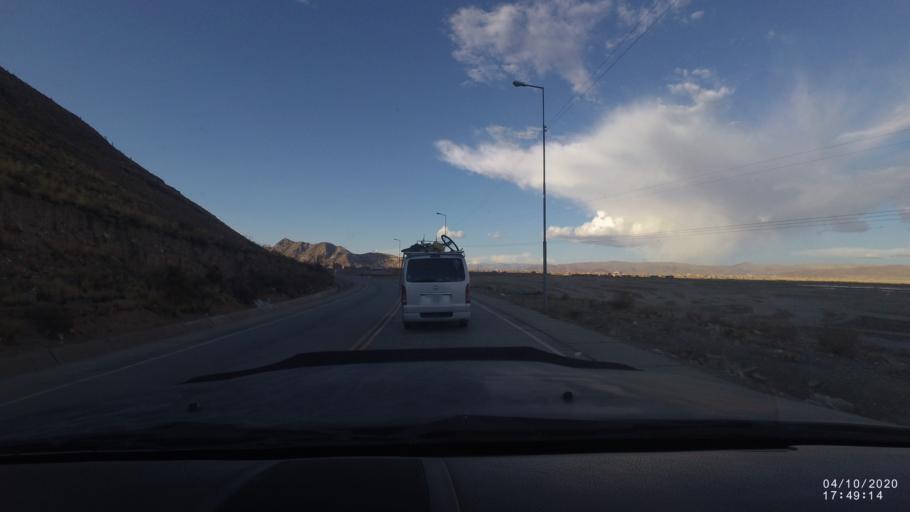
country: BO
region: Oruro
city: Oruro
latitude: -18.0132
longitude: -67.1375
